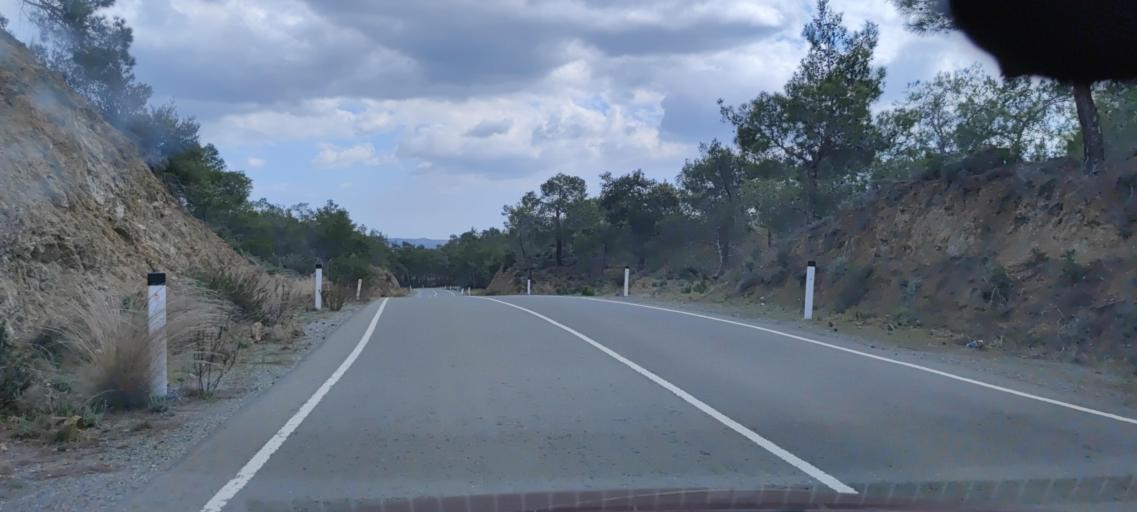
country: CY
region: Lefkosia
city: Lythrodontas
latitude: 34.9376
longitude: 33.3264
